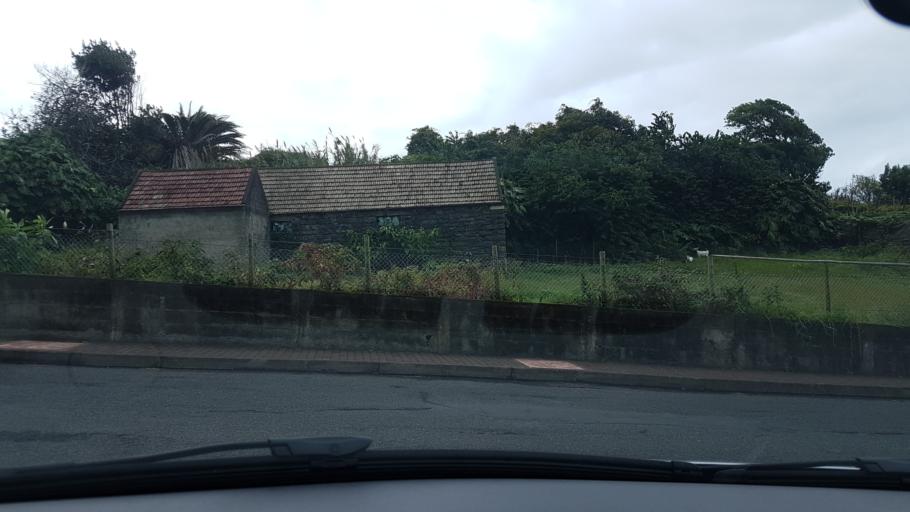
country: PT
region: Madeira
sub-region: Sao Vicente
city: Sao Vicente
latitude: 32.8246
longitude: -16.9888
